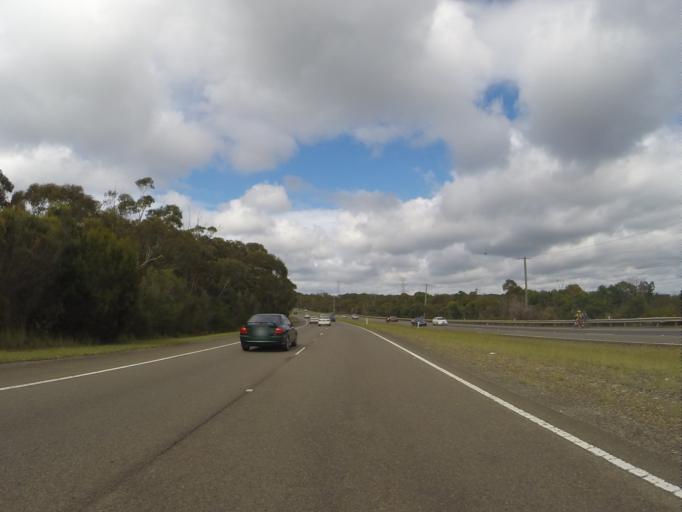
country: AU
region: New South Wales
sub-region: Sutherland Shire
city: Heathcote
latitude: -34.1130
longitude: 150.9924
